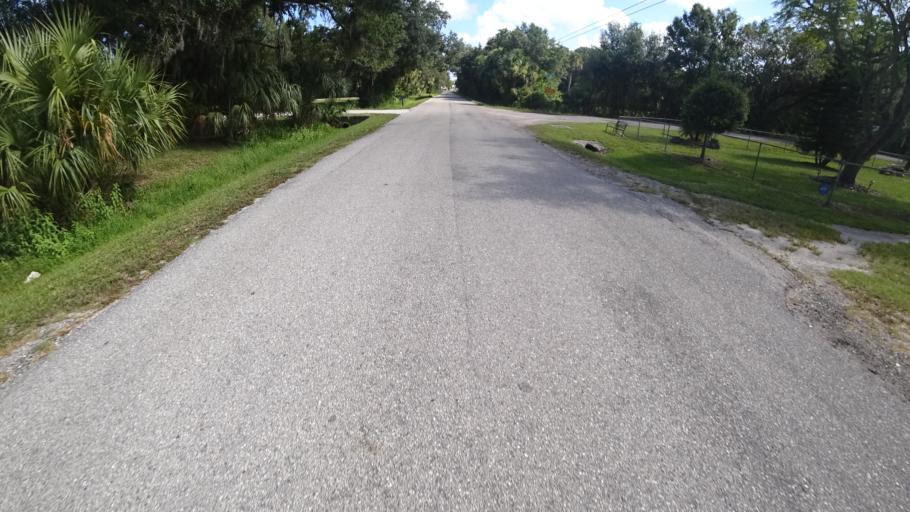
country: US
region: Florida
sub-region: Manatee County
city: Ellenton
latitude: 27.4885
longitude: -82.4794
